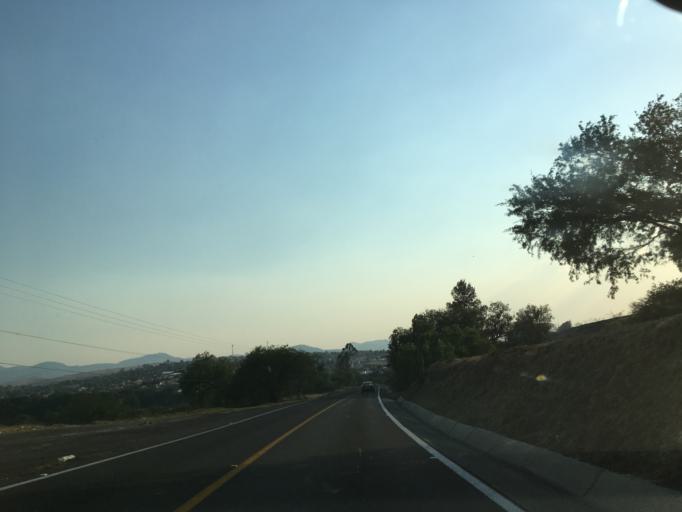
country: MX
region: Michoacan
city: Charo
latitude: 19.7573
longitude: -101.0366
